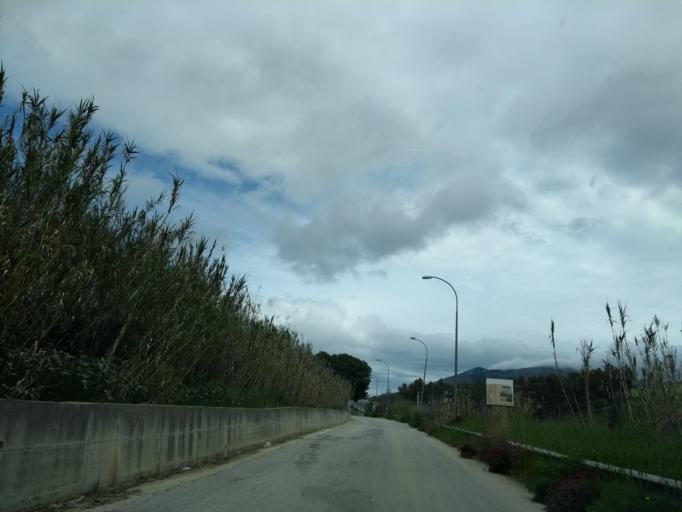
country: IT
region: Sicily
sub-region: Trapani
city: Calatafimi
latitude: 37.9450
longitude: 12.8323
